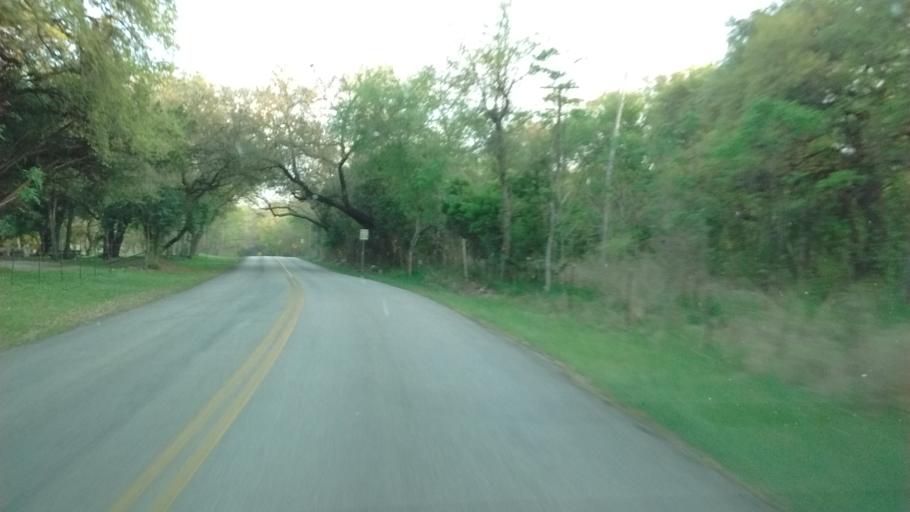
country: US
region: Texas
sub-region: Comal County
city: New Braunfels
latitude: 29.7586
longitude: -98.1403
